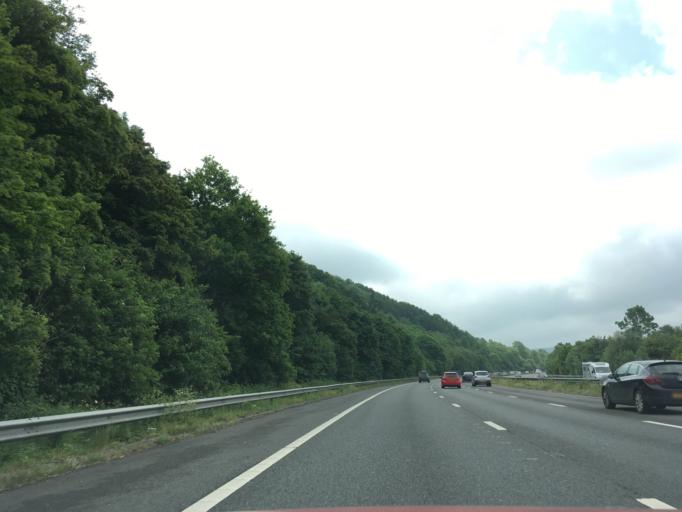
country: GB
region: England
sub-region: Devon
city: Cullompton
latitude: 50.8420
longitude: -3.3894
